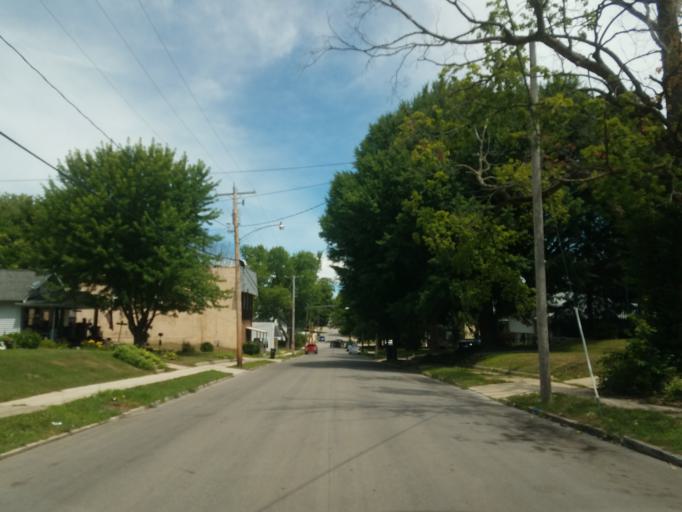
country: US
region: Illinois
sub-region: McLean County
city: Bloomington
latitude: 40.4726
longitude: -88.9857
